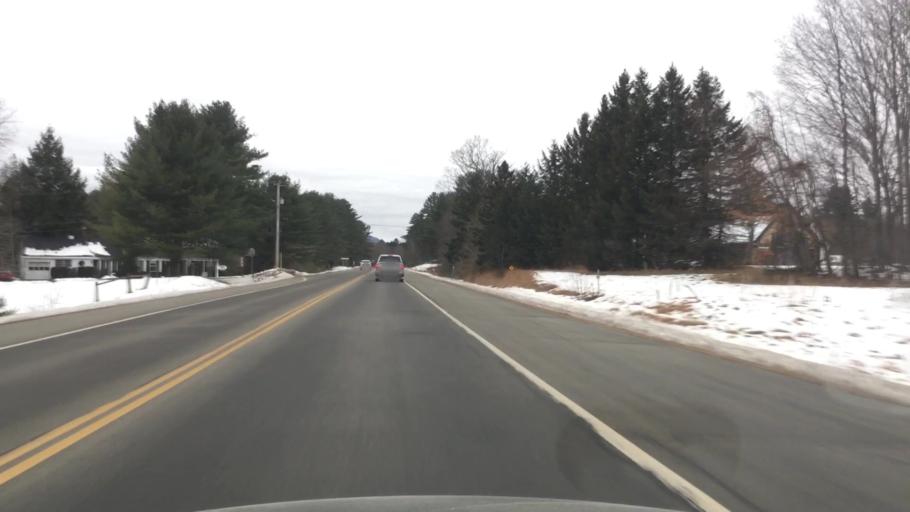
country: US
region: New Hampshire
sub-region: Merrimack County
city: Sutton
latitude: 43.2641
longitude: -71.9518
